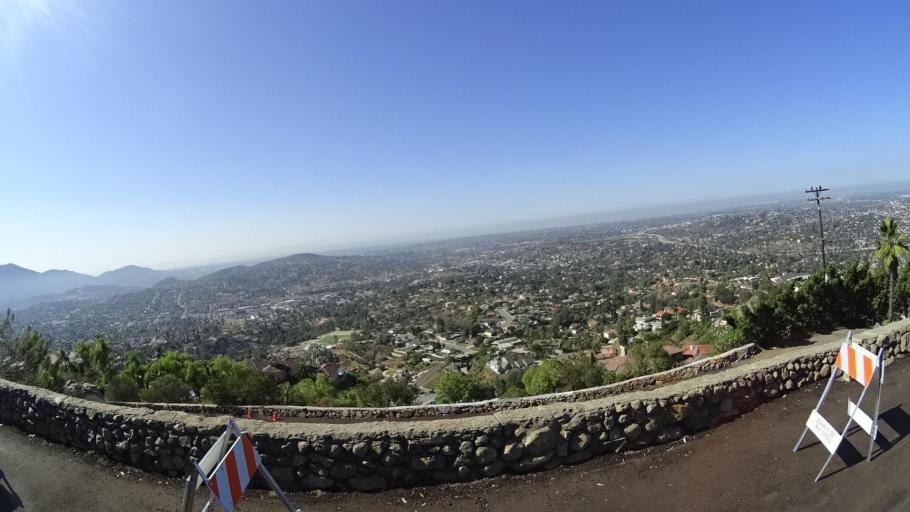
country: US
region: California
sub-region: San Diego County
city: Casa de Oro-Mount Helix
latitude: 32.7667
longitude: -116.9840
